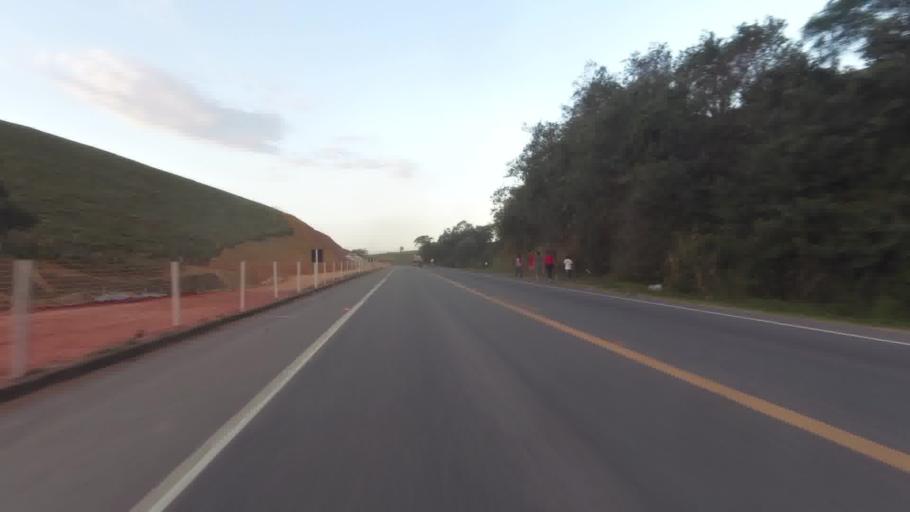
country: BR
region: Espirito Santo
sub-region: Iconha
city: Iconha
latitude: -20.7305
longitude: -40.7451
